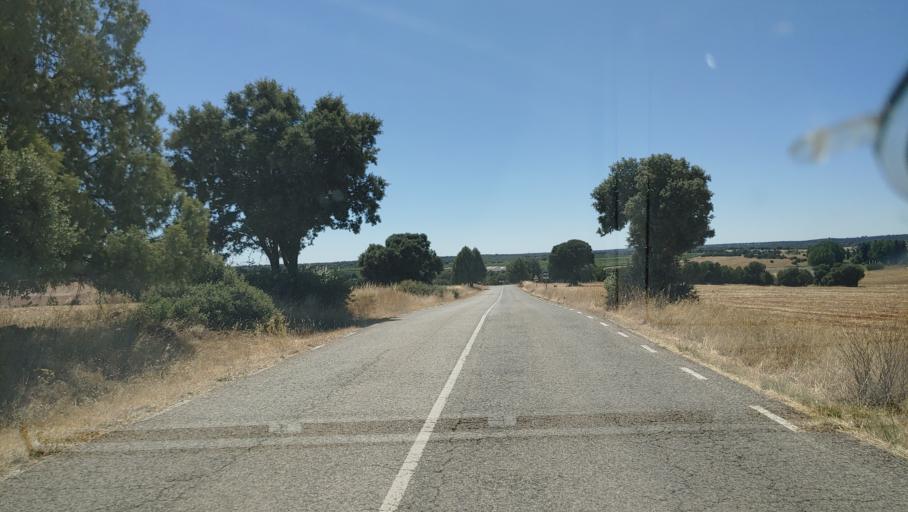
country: ES
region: Castille-La Mancha
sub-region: Provincia de Albacete
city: Ossa de Montiel
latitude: 38.9047
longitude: -2.7606
